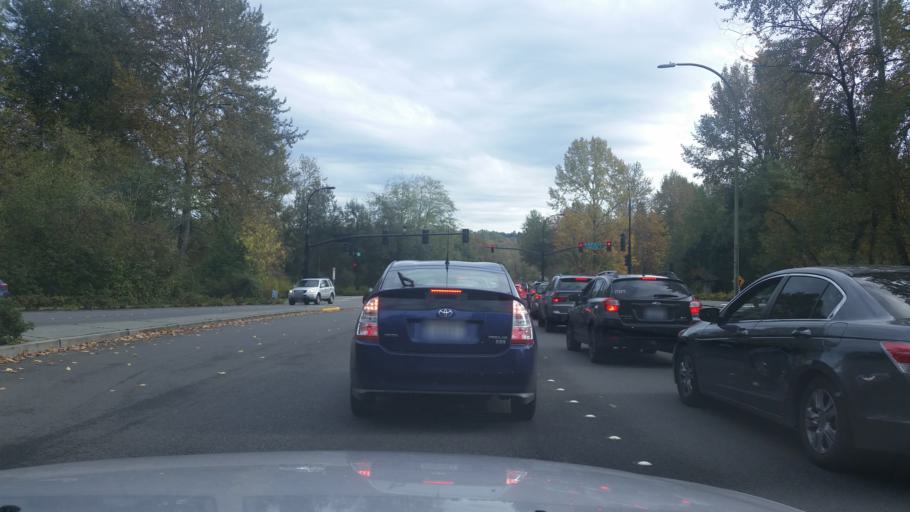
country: US
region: Washington
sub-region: King County
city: Bellevue
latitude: 47.6042
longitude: -122.1778
